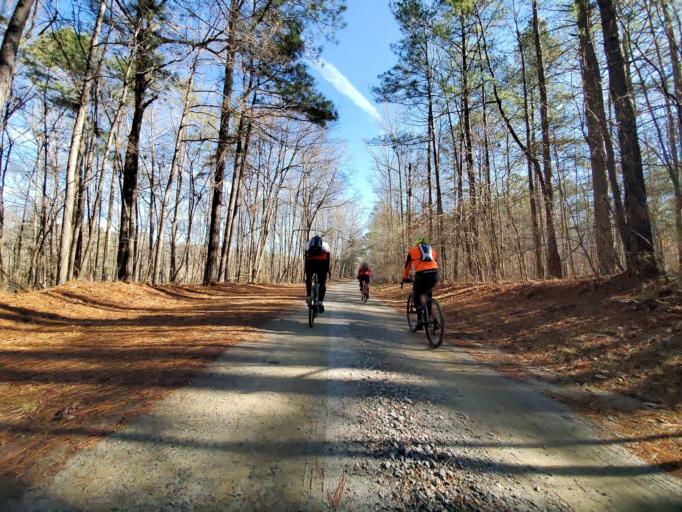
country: US
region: Georgia
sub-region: Fulton County
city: Chattahoochee Hills
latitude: 33.5727
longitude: -84.8009
